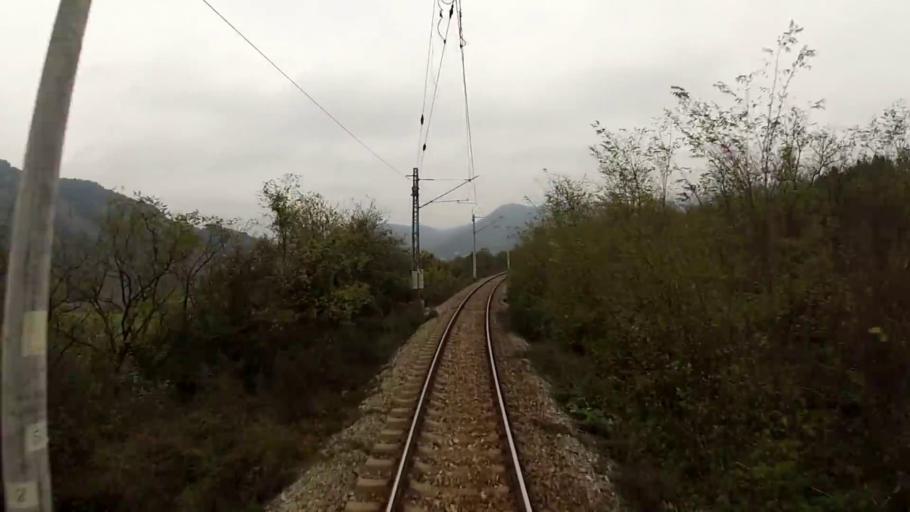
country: RS
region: Central Serbia
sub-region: Pirotski Okrug
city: Dimitrovgrad
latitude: 42.9878
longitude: 22.8515
